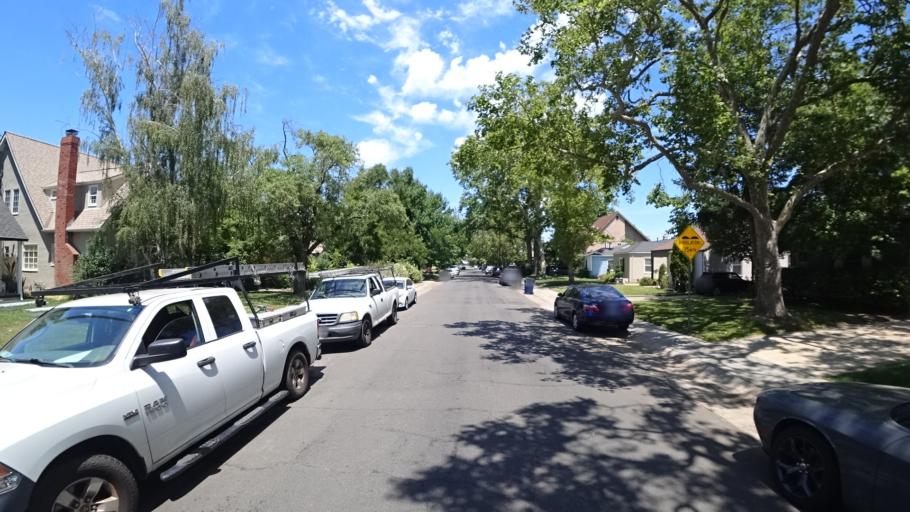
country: US
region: California
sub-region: Sacramento County
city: Sacramento
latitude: 38.5624
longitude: -121.4347
